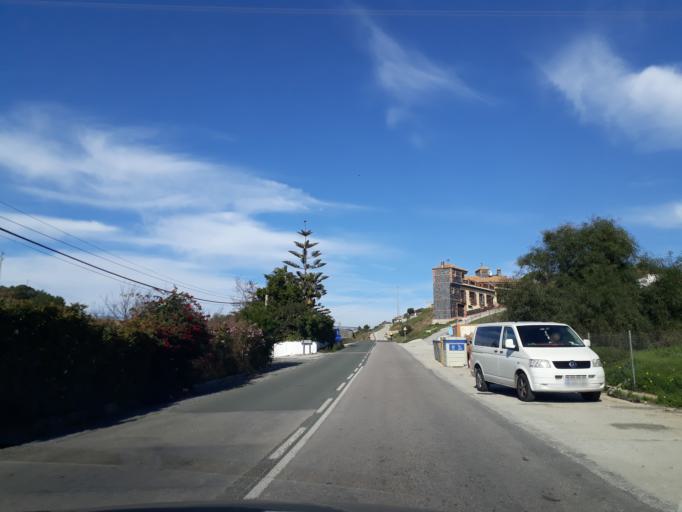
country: ES
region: Andalusia
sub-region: Provincia de Malaga
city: Fuengirola
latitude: 36.5202
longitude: -4.6845
